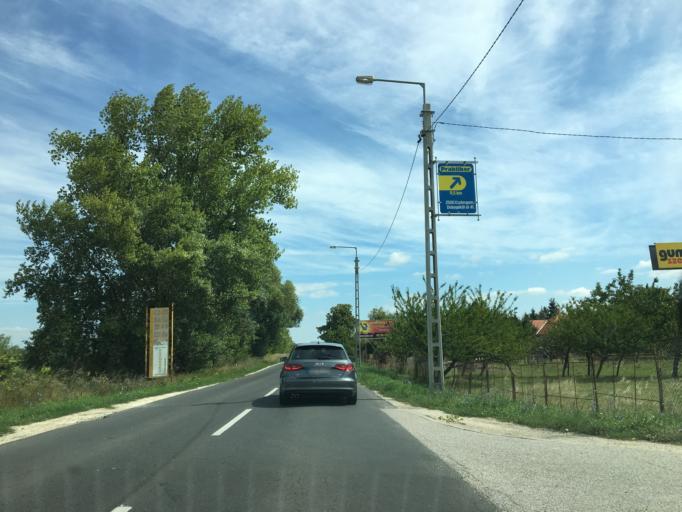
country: HU
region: Komarom-Esztergom
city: Tat
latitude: 47.7426
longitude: 18.6605
